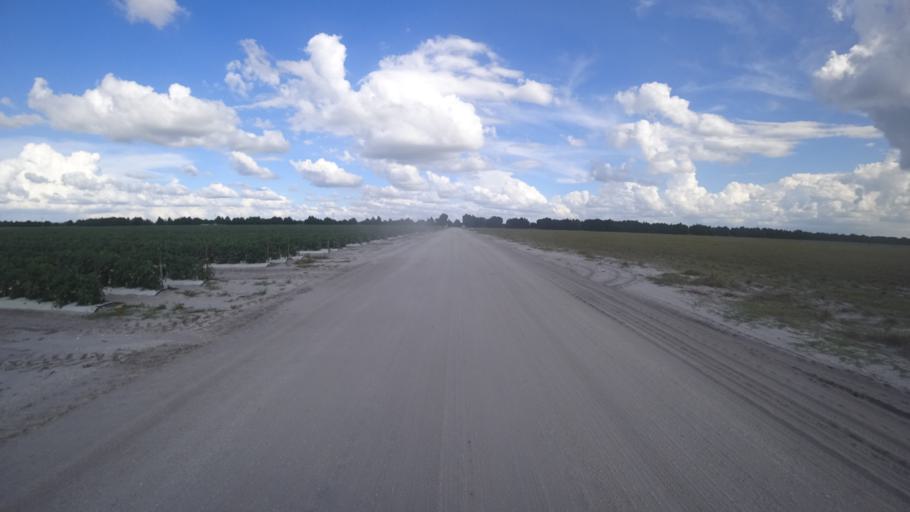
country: US
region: Florida
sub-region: DeSoto County
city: Arcadia
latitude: 27.2993
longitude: -82.1163
